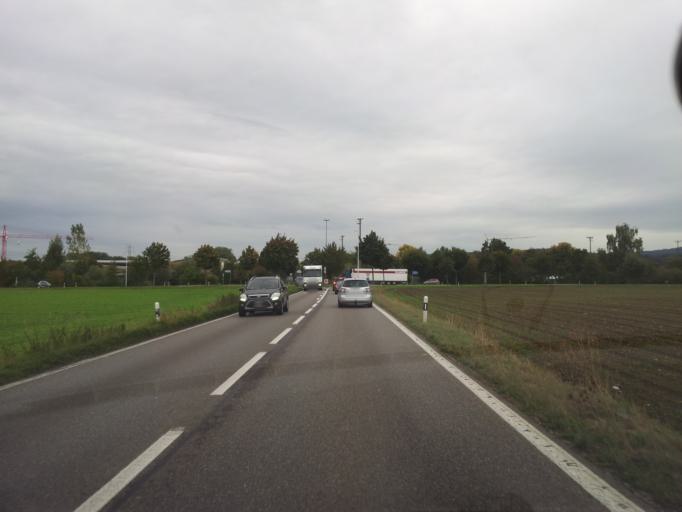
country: CH
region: Aargau
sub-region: Bezirk Bremgarten
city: Villmergen
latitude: 47.3573
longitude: 8.2445
